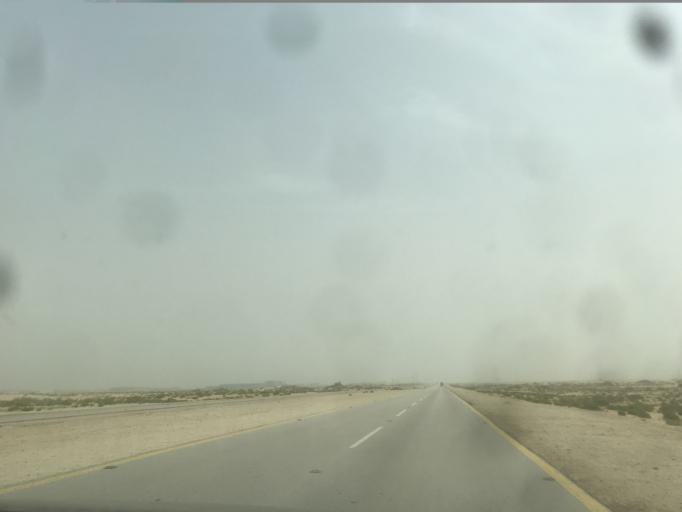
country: SA
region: Eastern Province
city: Abqaiq
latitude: 25.9092
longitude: 49.9343
